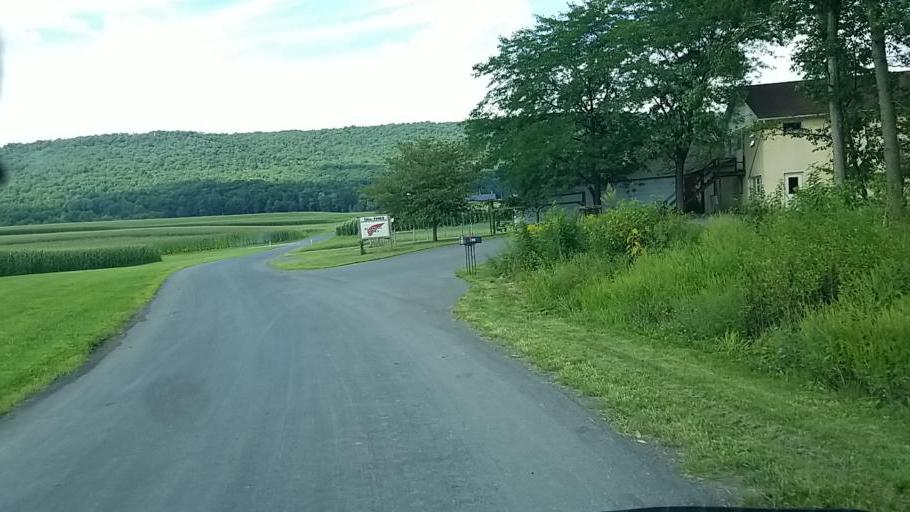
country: US
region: Pennsylvania
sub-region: Dauphin County
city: Elizabethville
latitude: 40.6039
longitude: -76.8516
